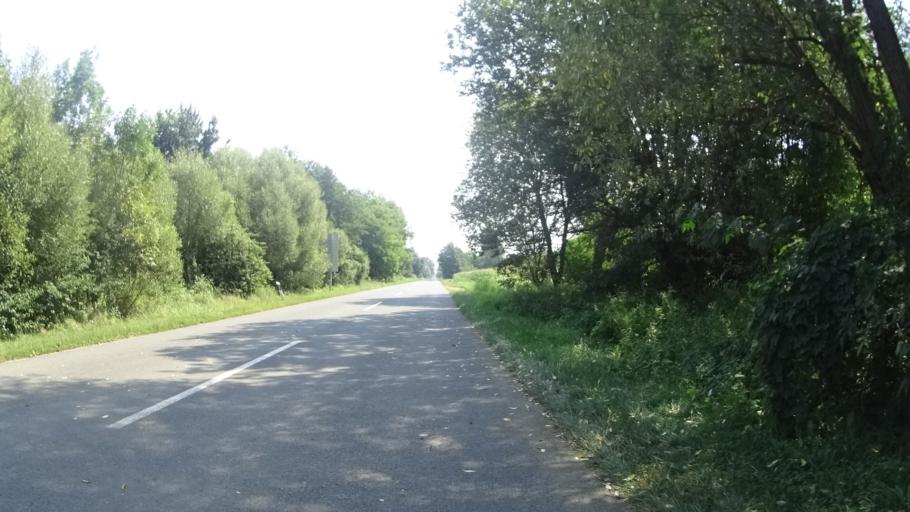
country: HR
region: Medimurska
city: Hodosan
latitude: 46.4055
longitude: 16.6655
